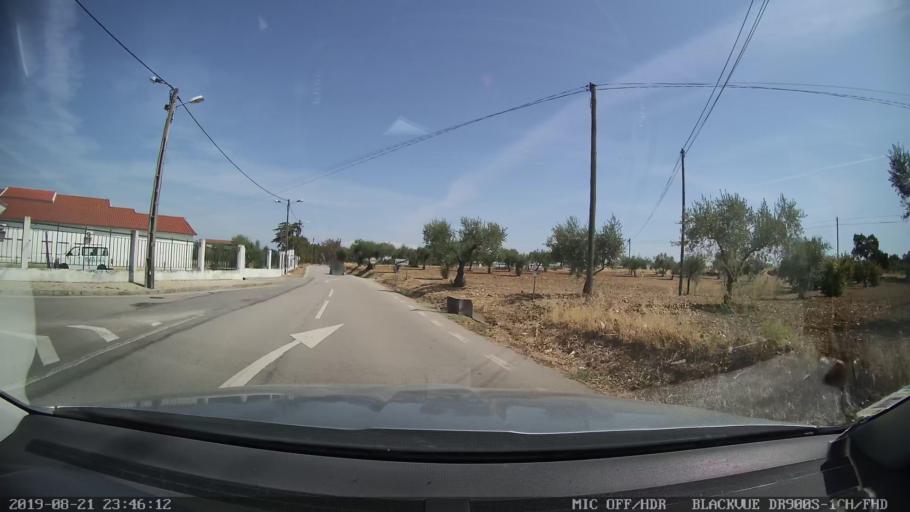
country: PT
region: Castelo Branco
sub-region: Idanha-A-Nova
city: Idanha-a-Nova
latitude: 39.8396
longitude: -7.2592
